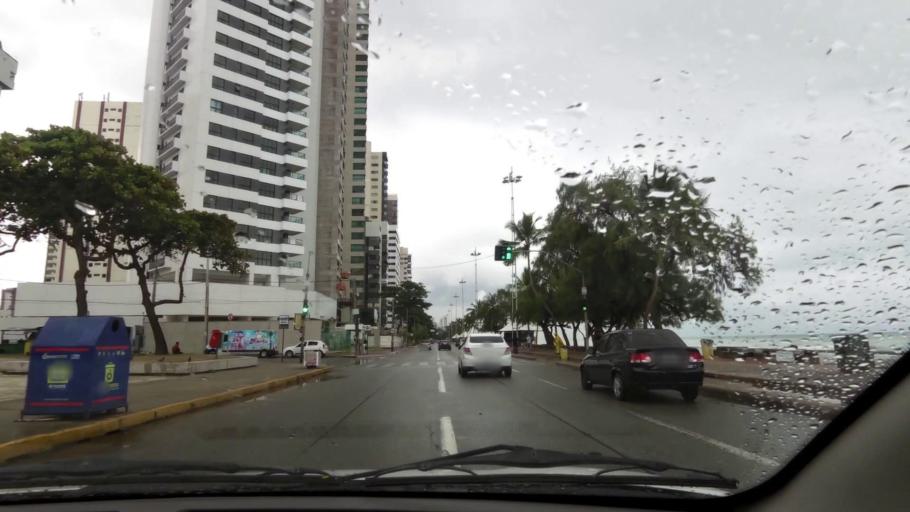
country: BR
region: Pernambuco
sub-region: Recife
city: Recife
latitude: -8.1323
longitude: -34.9001
